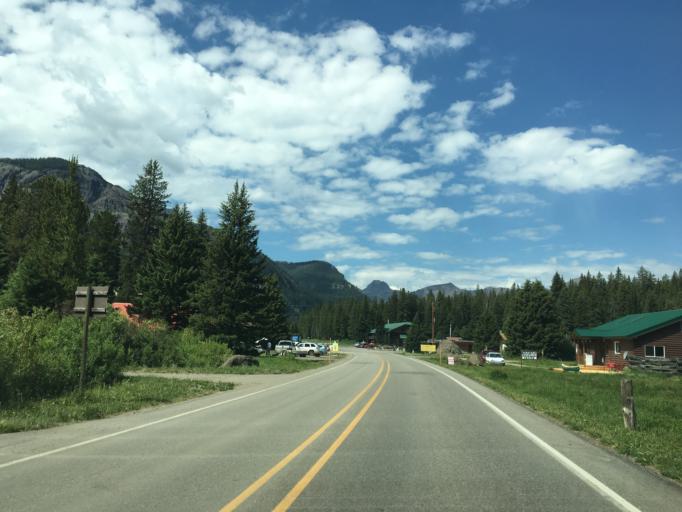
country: US
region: Montana
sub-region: Stillwater County
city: Absarokee
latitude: 45.0076
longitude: -109.9881
